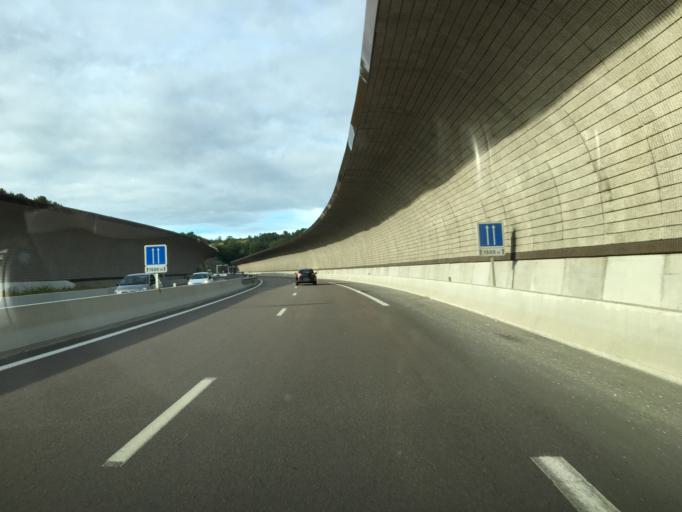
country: FR
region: Bourgogne
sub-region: Departement de la Cote-d'Or
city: Plombieres-les-Dijon
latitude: 47.3371
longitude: 4.9855
